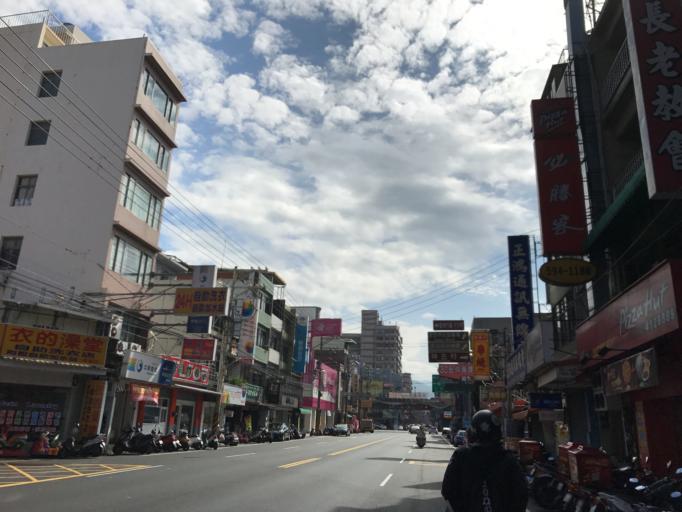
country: TW
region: Taiwan
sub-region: Hsinchu
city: Zhubei
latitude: 24.7428
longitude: 121.0842
